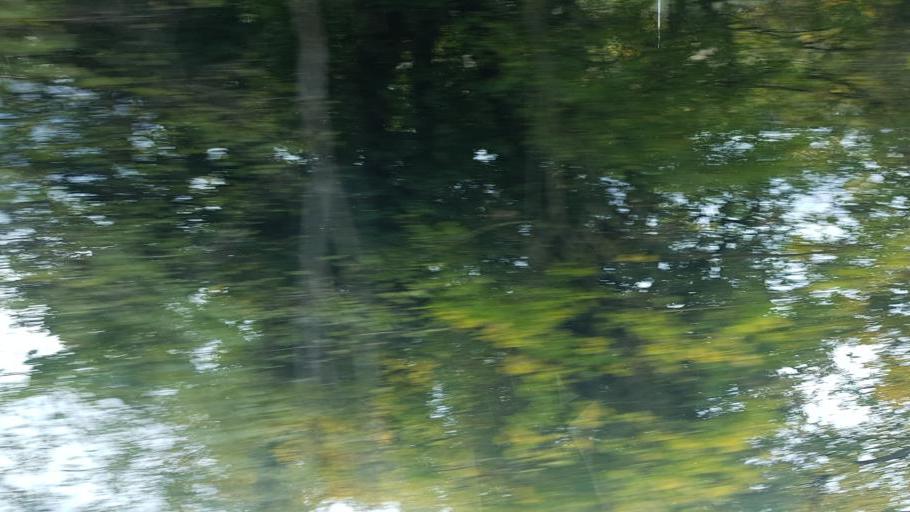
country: IT
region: Abruzzo
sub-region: Provincia dell' Aquila
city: Progetto Case Bazzano
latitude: 42.3562
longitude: 13.4283
